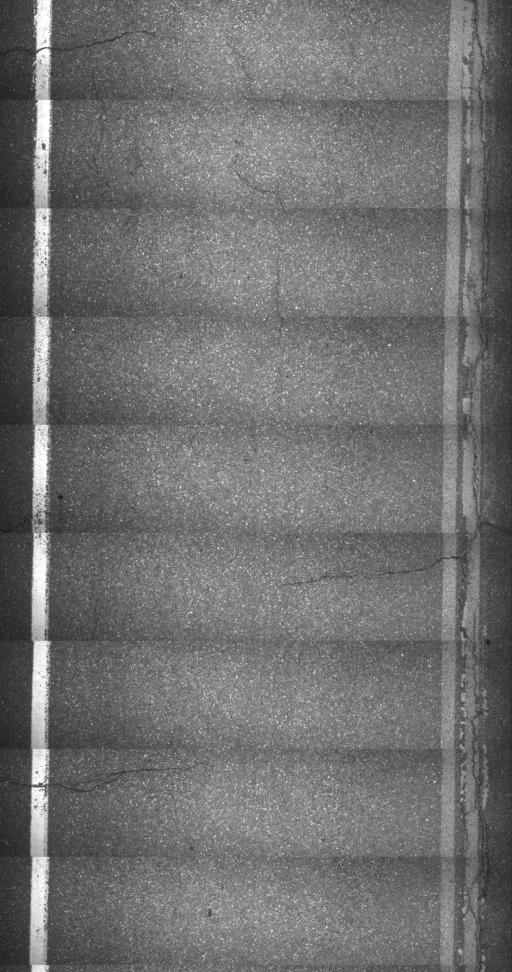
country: US
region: Vermont
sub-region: Caledonia County
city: Saint Johnsbury
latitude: 44.3994
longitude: -72.0254
